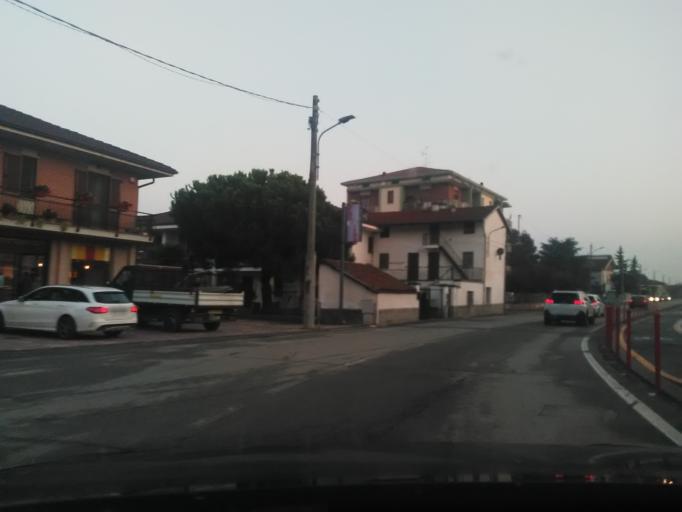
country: IT
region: Piedmont
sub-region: Provincia di Vercelli
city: Carisio
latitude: 45.4087
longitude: 8.1983
